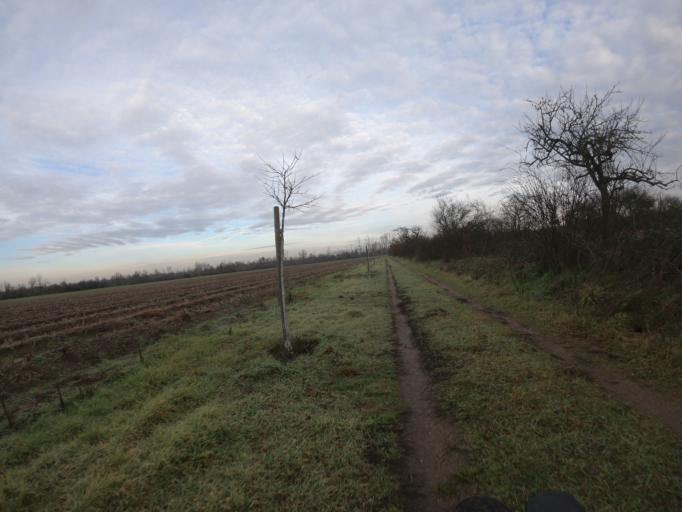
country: DE
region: Hesse
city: Morfelden-Walldorf
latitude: 49.9711
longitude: 8.5859
